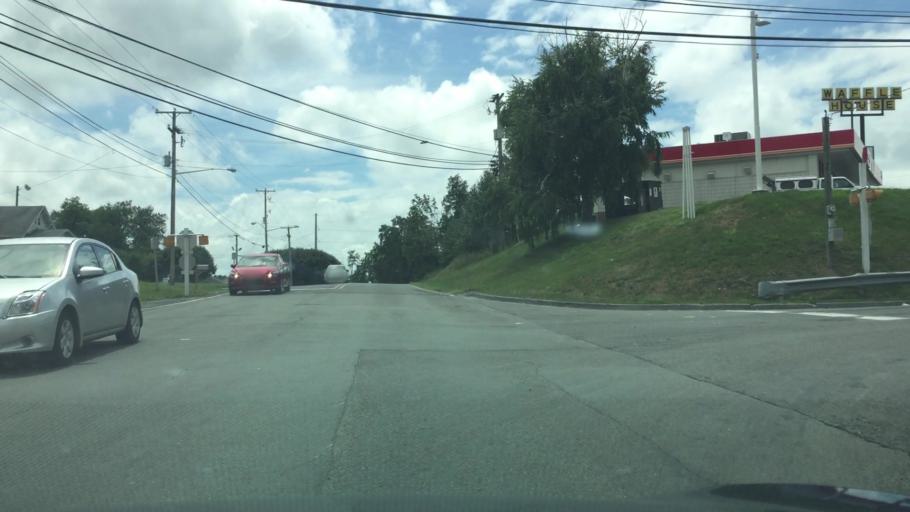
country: US
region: Virginia
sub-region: Wythe County
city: Wytheville
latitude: 36.9475
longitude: -81.0562
